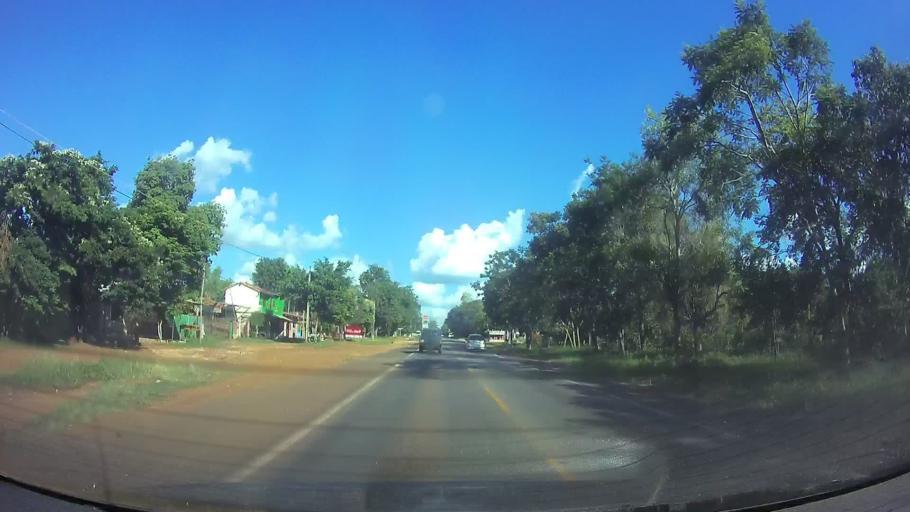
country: PY
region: Cordillera
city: Eusebio Ayala
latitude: -25.3943
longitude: -56.9547
